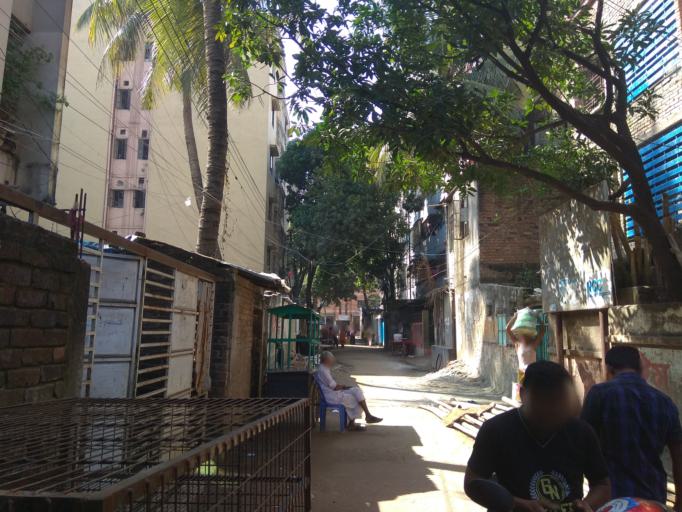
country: BD
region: Dhaka
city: Tungi
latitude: 23.8181
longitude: 90.3696
